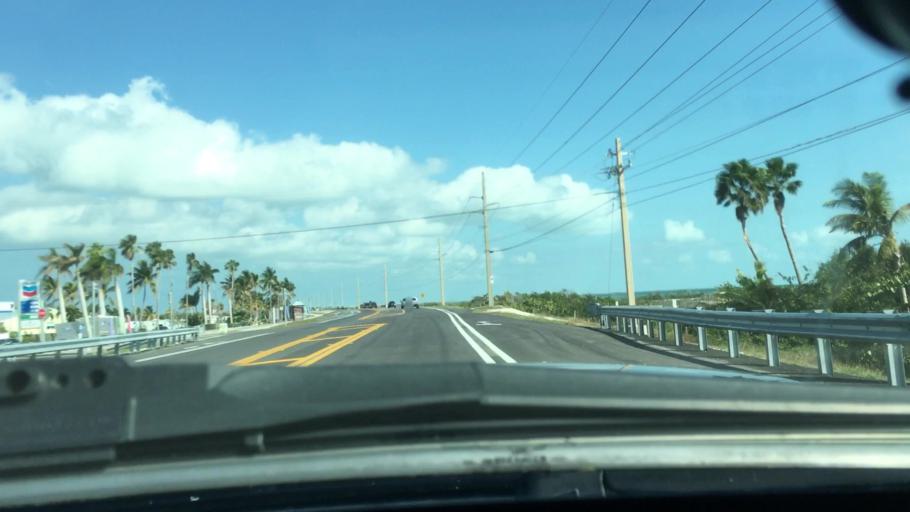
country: US
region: Florida
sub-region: Monroe County
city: Big Pine Key
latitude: 24.6711
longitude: -81.2478
